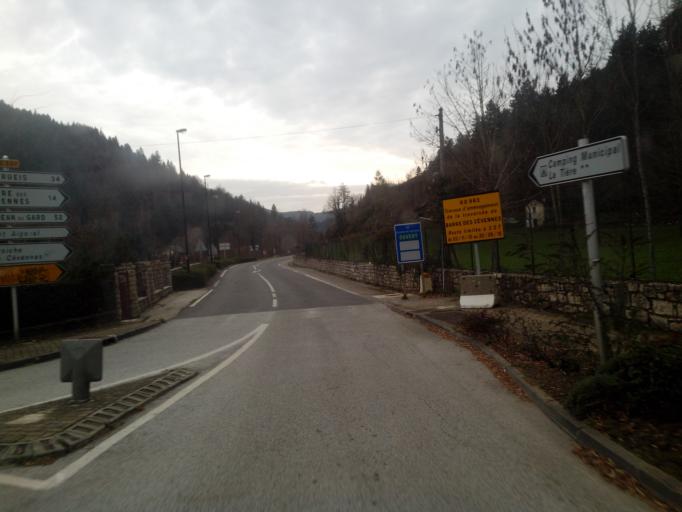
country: FR
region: Languedoc-Roussillon
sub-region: Departement de la Lozere
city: Florac
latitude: 44.3189
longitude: 3.5978
